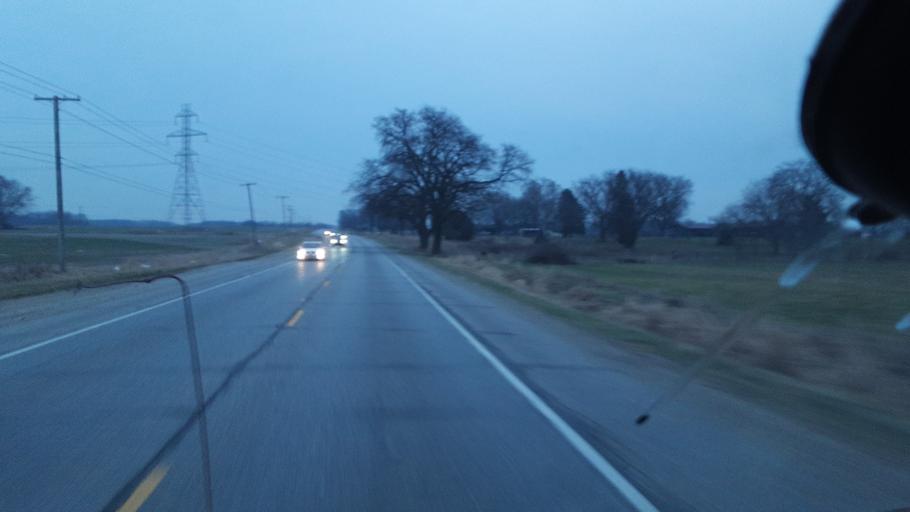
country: US
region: Indiana
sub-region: Elkhart County
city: Bristol
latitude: 41.6674
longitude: -85.7761
